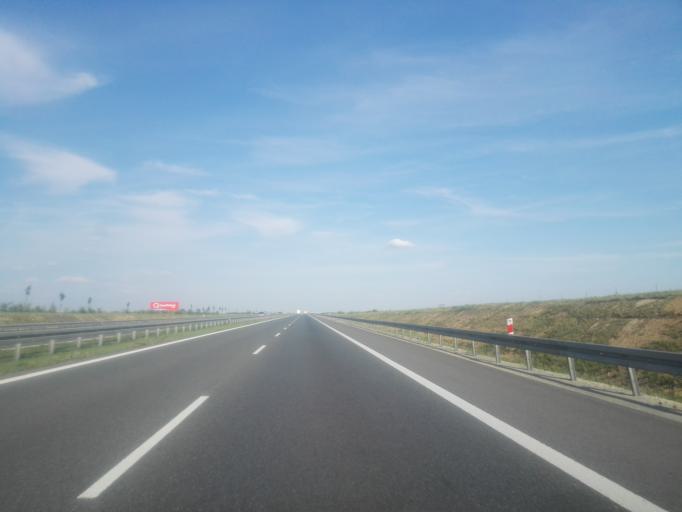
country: PL
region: Lower Silesian Voivodeship
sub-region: Powiat olesnicki
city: Dobroszyce
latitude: 51.2268
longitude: 17.2717
